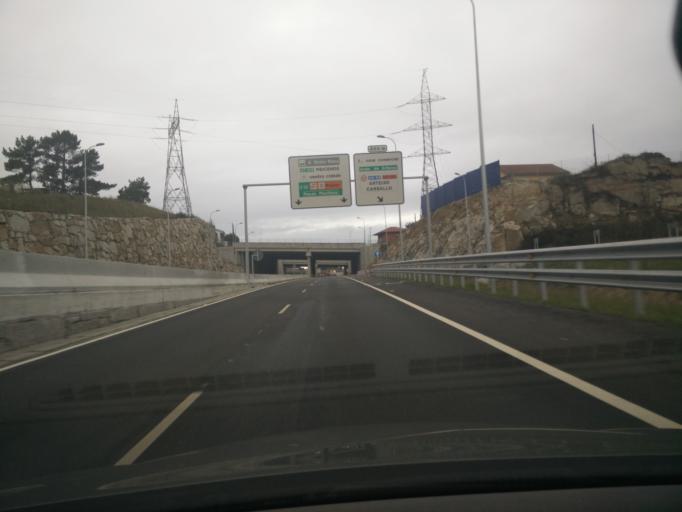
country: ES
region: Galicia
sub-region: Provincia da Coruna
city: A Coruna
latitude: 43.3388
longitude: -8.4239
